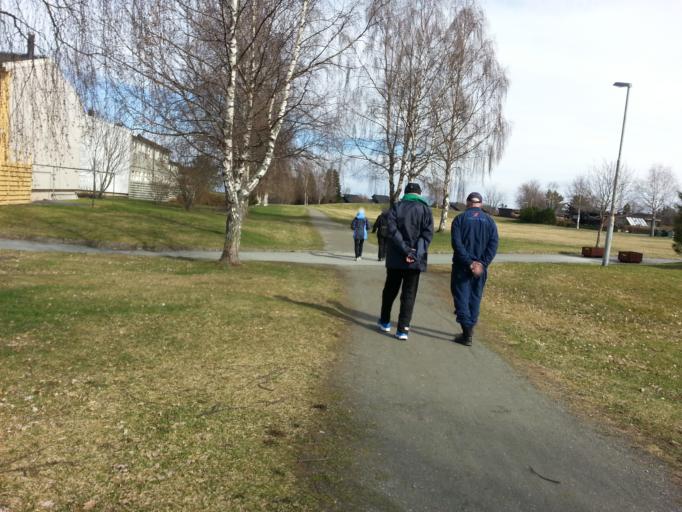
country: NO
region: Sor-Trondelag
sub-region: Trondheim
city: Trondheim
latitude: 63.4258
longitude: 10.4478
